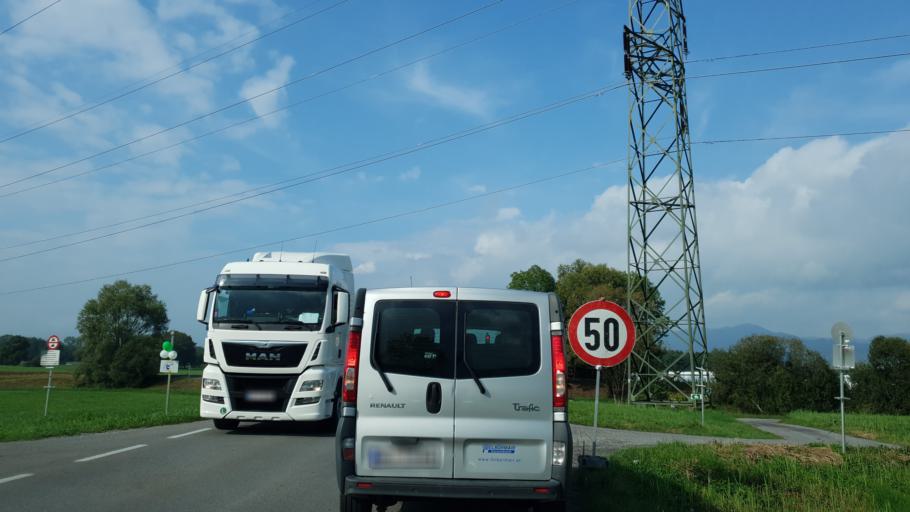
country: AT
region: Vorarlberg
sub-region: Politischer Bezirk Dornbirn
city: Hohenems
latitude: 47.3993
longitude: 9.6864
